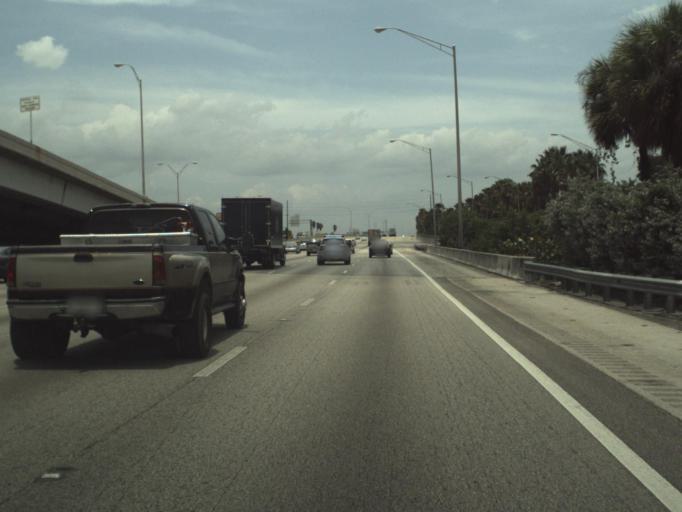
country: US
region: Florida
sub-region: Broward County
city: Boulevard Gardens
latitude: 26.1240
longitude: -80.1687
